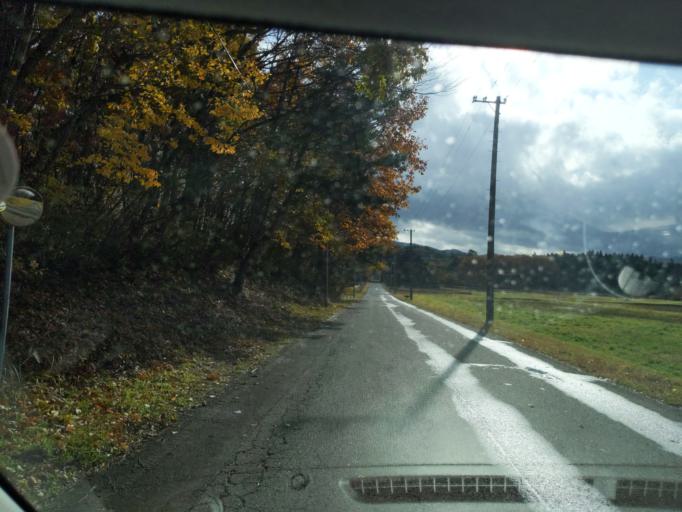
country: JP
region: Iwate
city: Mizusawa
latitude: 39.1090
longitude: 140.9723
